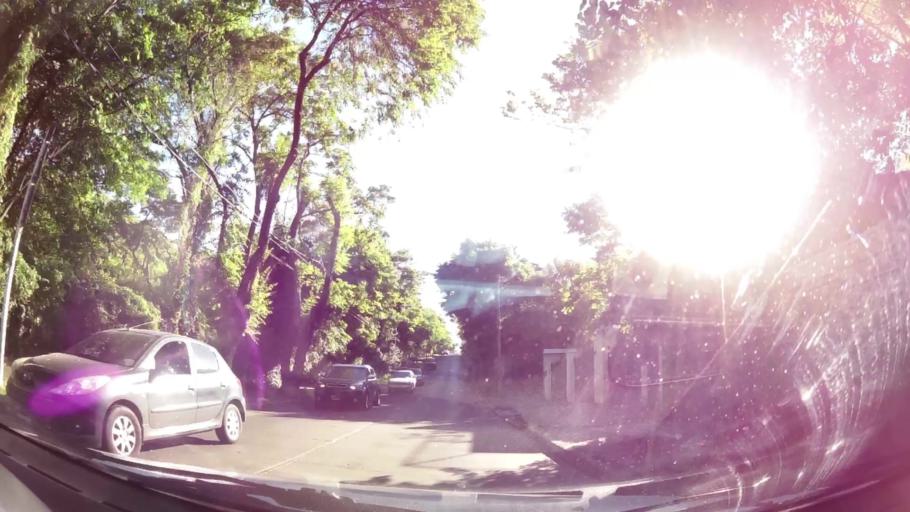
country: AR
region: Buenos Aires
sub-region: Partido de San Isidro
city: San Isidro
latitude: -34.4691
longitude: -58.5025
